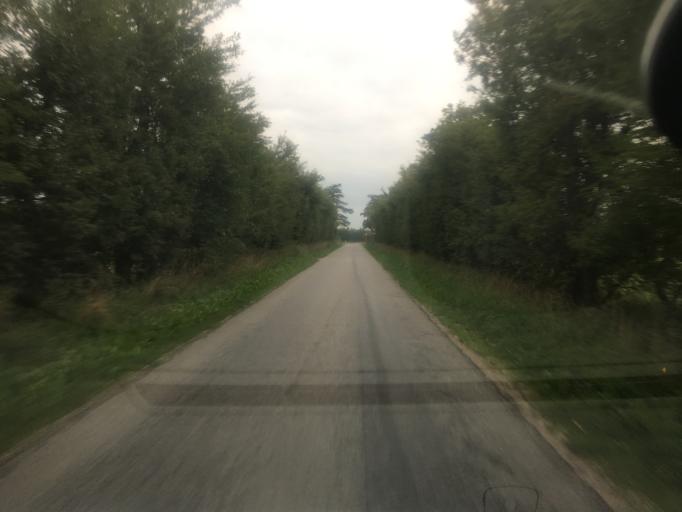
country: DK
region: South Denmark
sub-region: Tonder Kommune
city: Logumkloster
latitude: 55.0402
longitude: 9.0083
